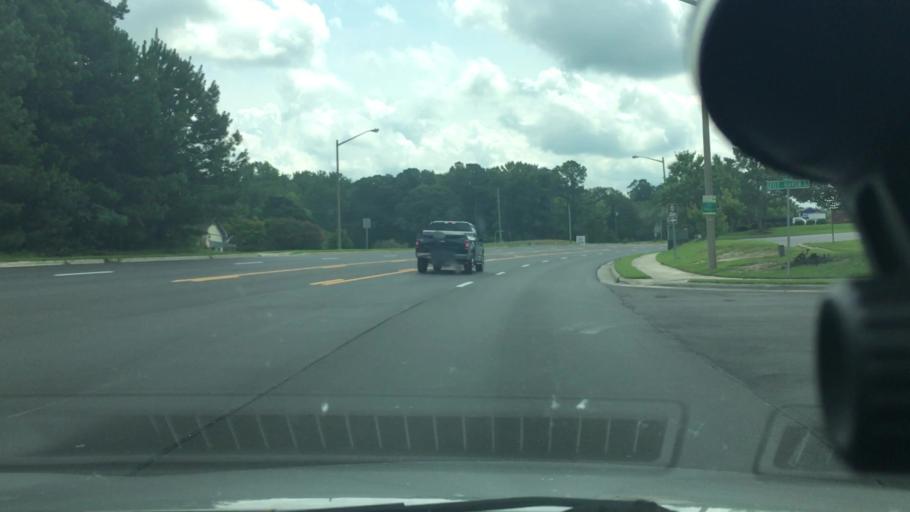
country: US
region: North Carolina
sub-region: Pitt County
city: Greenville
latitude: 35.5922
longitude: -77.3190
